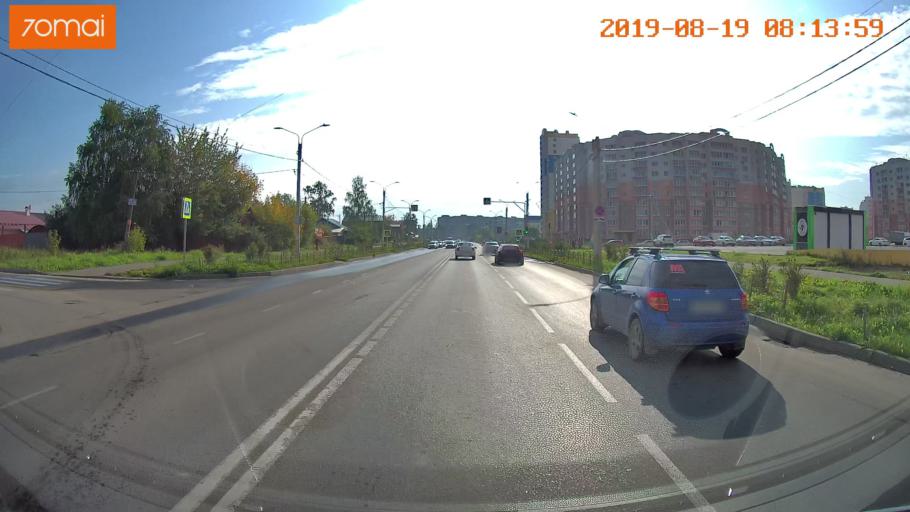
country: RU
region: Ivanovo
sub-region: Gorod Ivanovo
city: Ivanovo
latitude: 56.9713
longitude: 40.9841
